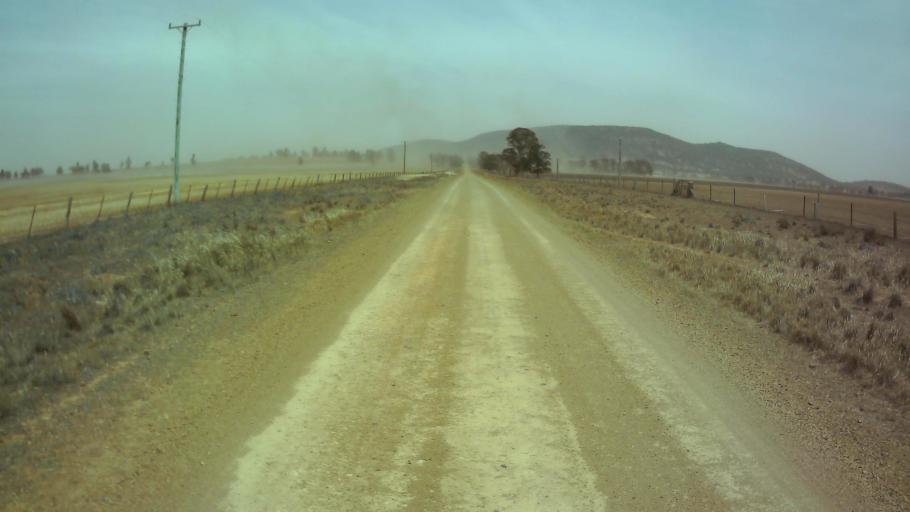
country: AU
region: New South Wales
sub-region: Weddin
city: Grenfell
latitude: -33.7463
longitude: 147.9829
